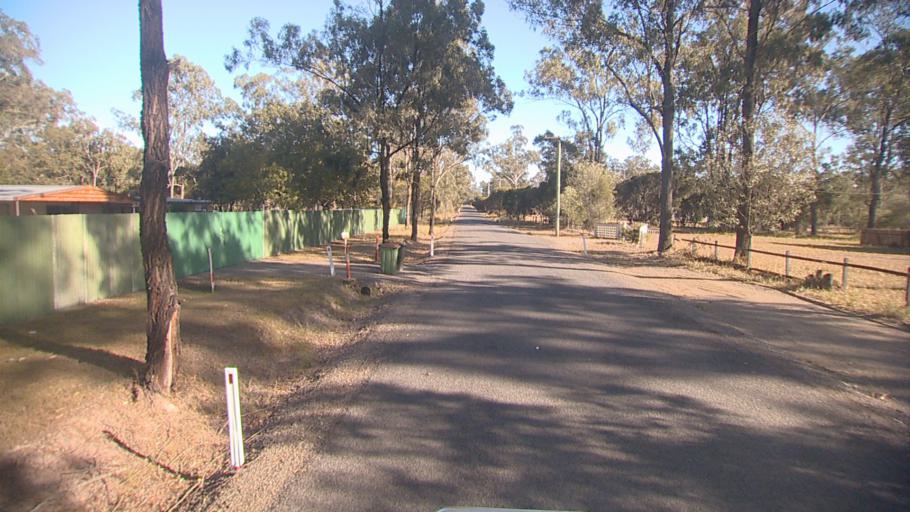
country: AU
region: Queensland
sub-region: Logan
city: Cedar Vale
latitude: -27.8390
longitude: 153.0017
